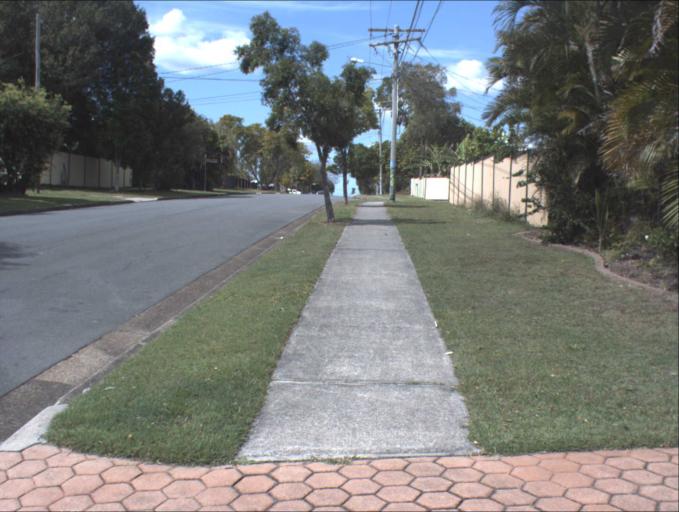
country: AU
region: Queensland
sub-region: Logan
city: Logan Reserve
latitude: -27.6804
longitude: 153.0826
